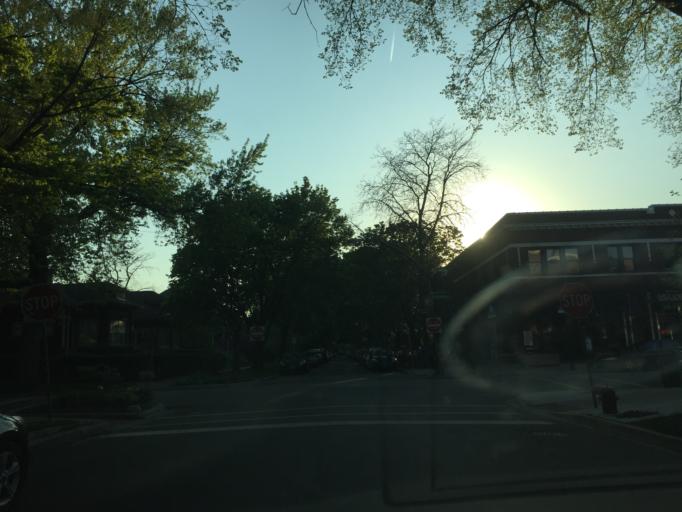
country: US
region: Illinois
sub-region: Cook County
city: Lincolnwood
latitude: 41.9657
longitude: -87.6933
